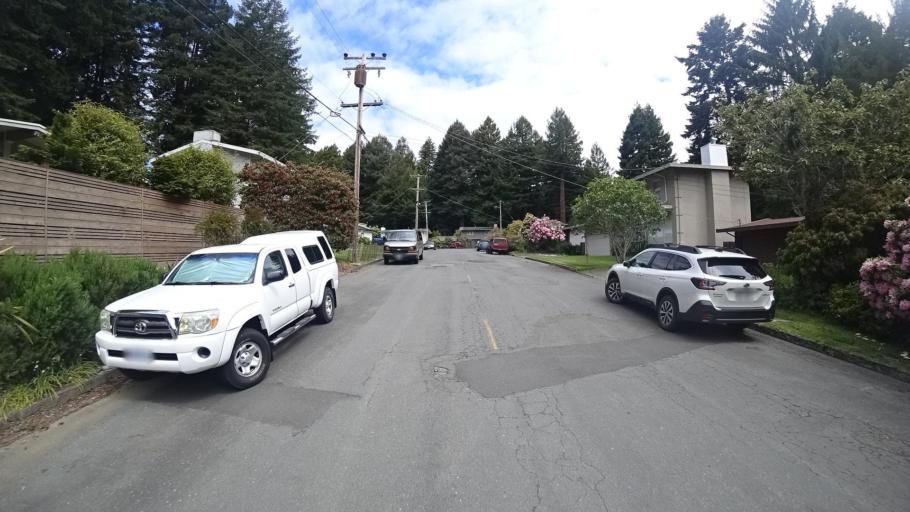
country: US
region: California
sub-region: Humboldt County
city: Arcata
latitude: 40.8636
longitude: -124.0694
